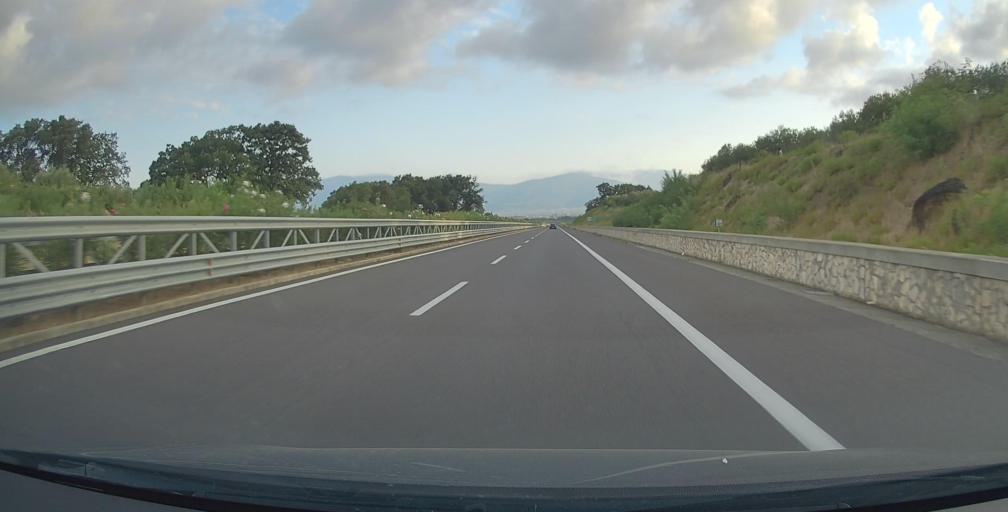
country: IT
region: Calabria
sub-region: Provincia di Catanzaro
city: Acconia
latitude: 38.8726
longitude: 16.2817
